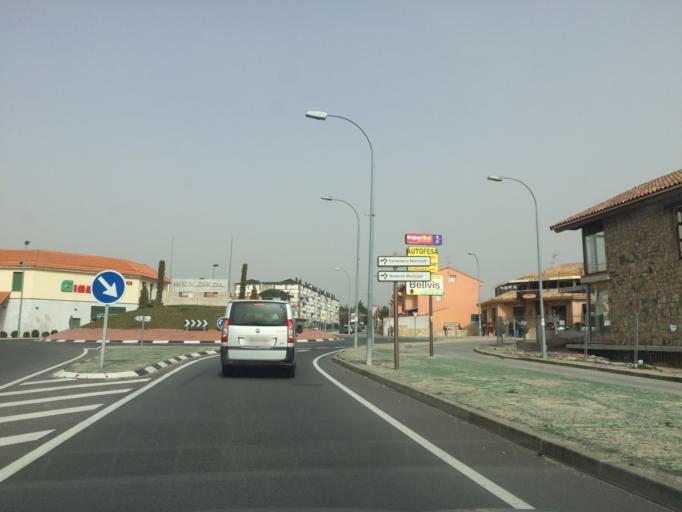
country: ES
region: Madrid
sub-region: Provincia de Madrid
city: Moralzarzal
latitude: 40.6719
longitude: -3.9731
